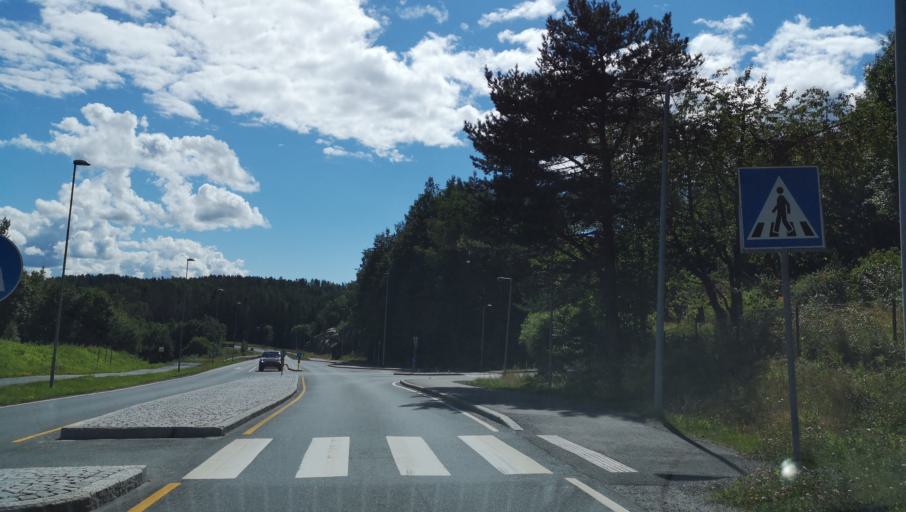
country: NO
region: Akershus
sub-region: Frogn
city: Drobak
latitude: 59.6675
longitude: 10.6595
